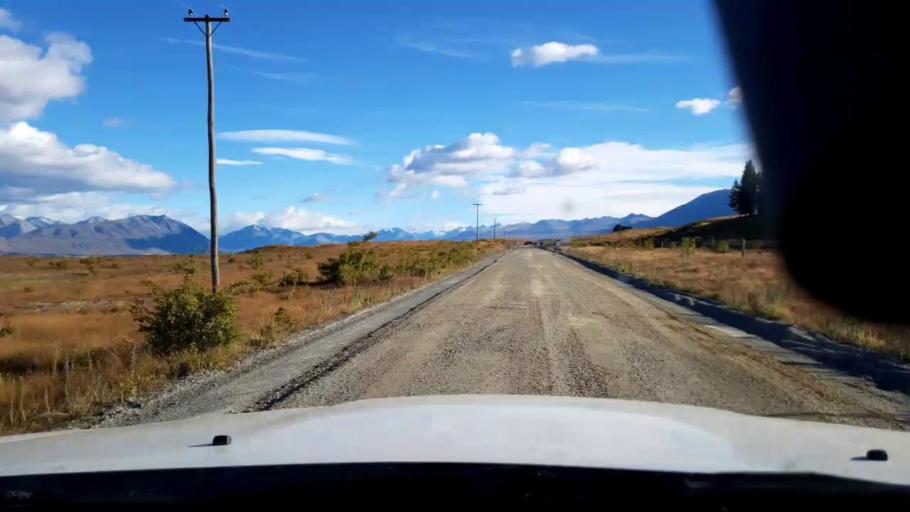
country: NZ
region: Canterbury
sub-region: Timaru District
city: Pleasant Point
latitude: -43.9819
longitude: 170.5083
